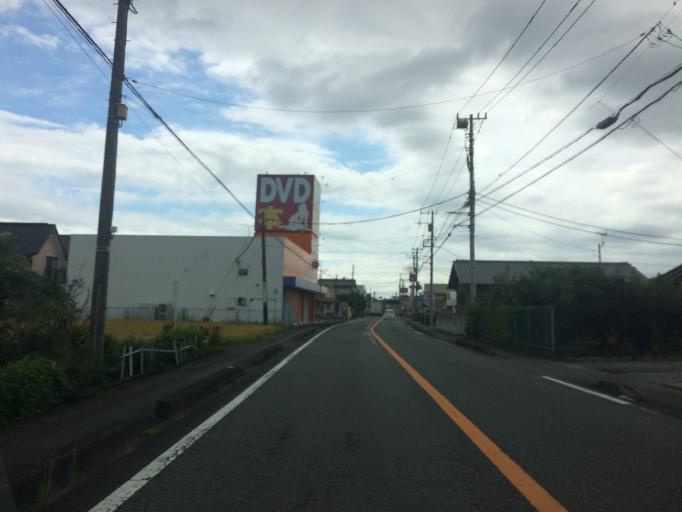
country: JP
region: Shizuoka
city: Fuji
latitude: 35.1740
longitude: 138.6480
